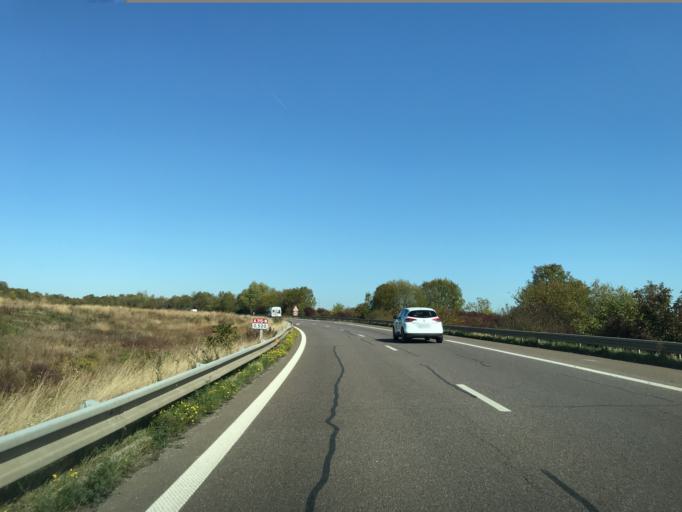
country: FR
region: Lorraine
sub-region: Departement de la Moselle
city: Saint-Julien-les-Metz
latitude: 49.1356
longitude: 6.2484
